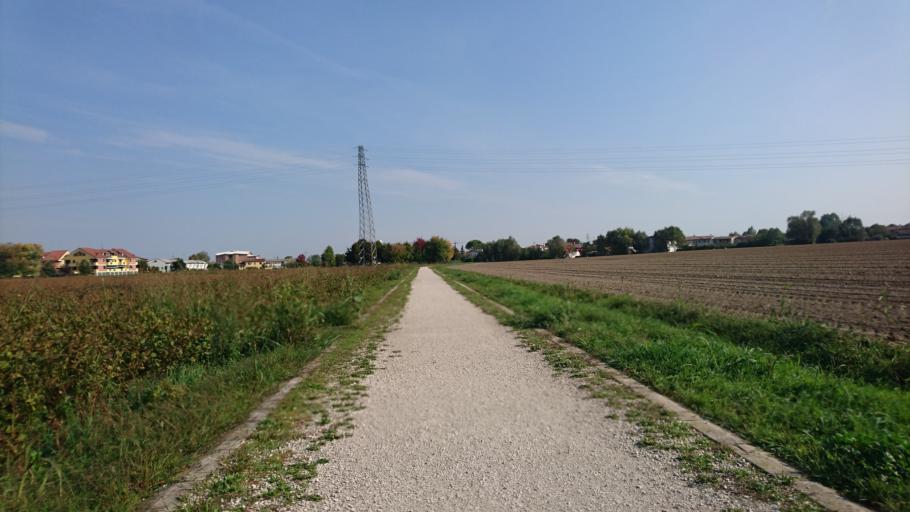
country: IT
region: Veneto
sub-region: Provincia di Padova
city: Sarmeola
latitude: 45.4250
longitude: 11.8458
